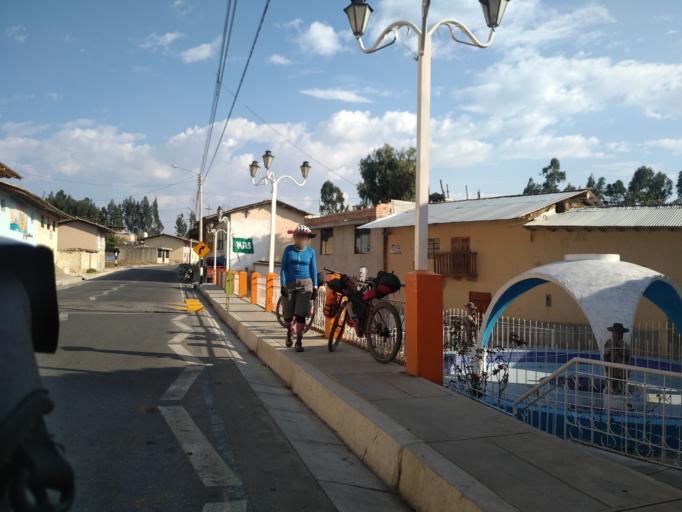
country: PE
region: Cajamarca
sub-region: San Marcos
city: San Marcos
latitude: -7.3866
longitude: -78.1243
